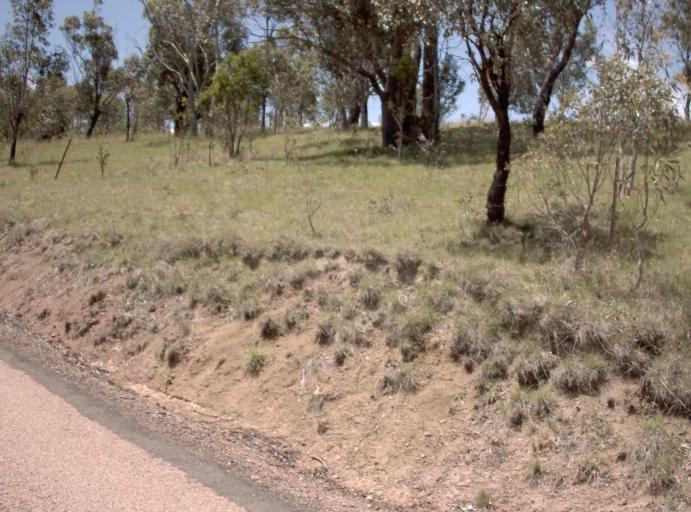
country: AU
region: New South Wales
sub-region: Snowy River
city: Jindabyne
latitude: -37.1033
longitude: 148.2504
